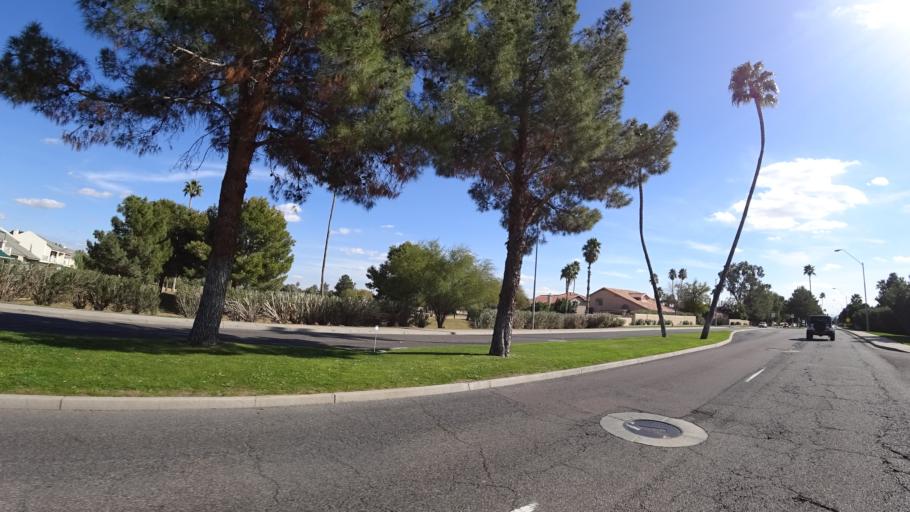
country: US
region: Arizona
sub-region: Maricopa County
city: Sun City
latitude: 33.6629
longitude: -112.2205
